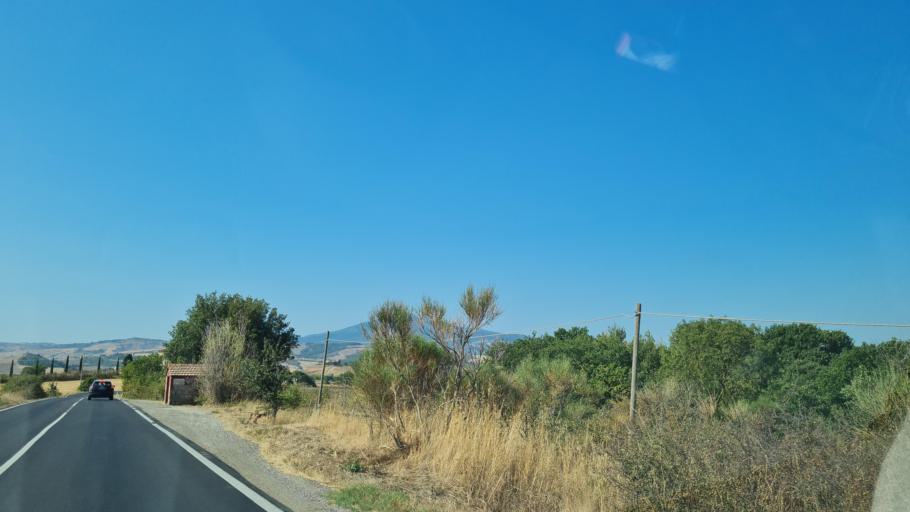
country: IT
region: Tuscany
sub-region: Provincia di Siena
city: Chianciano Terme
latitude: 43.0136
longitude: 11.7645
